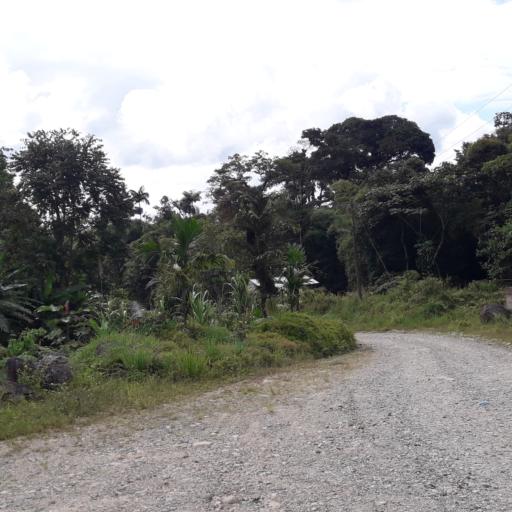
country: EC
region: Napo
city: Archidona
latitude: -0.9460
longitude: -77.8908
